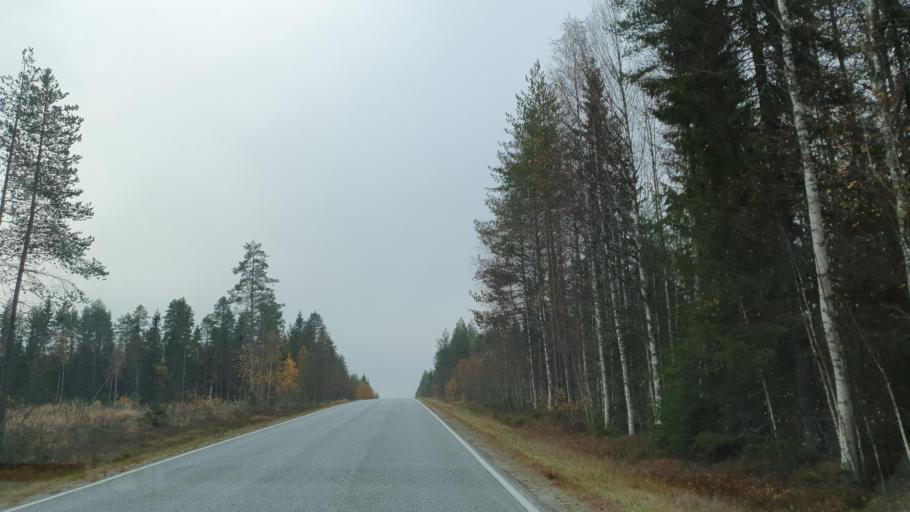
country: FI
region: Kainuu
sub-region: Kehys-Kainuu
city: Kuhmo
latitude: 64.4085
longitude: 29.4751
